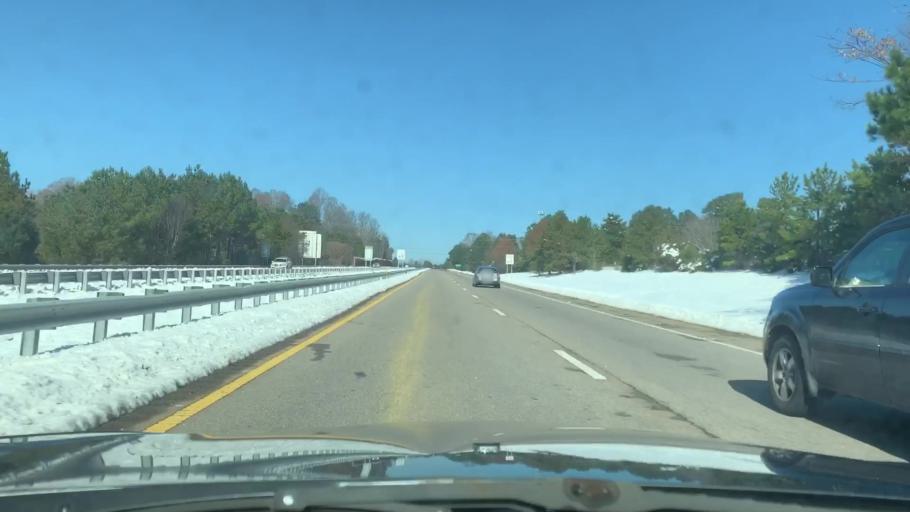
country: US
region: North Carolina
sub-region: Durham County
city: Durham
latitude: 36.0241
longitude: -78.9591
